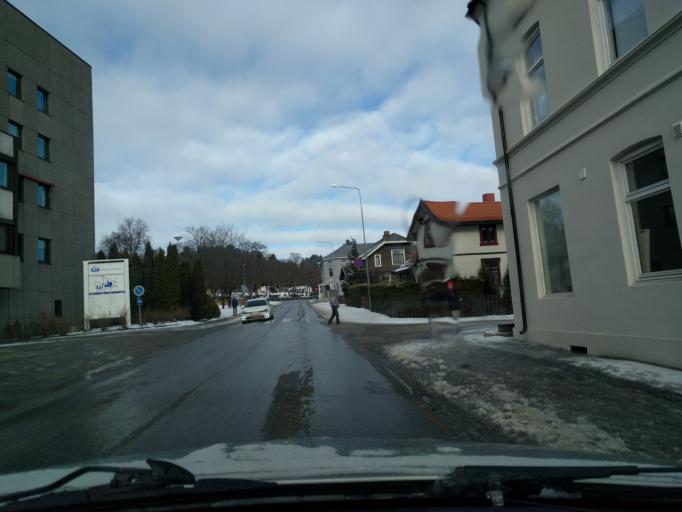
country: NO
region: Hedmark
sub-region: Hamar
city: Hamar
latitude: 60.7983
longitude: 11.0725
